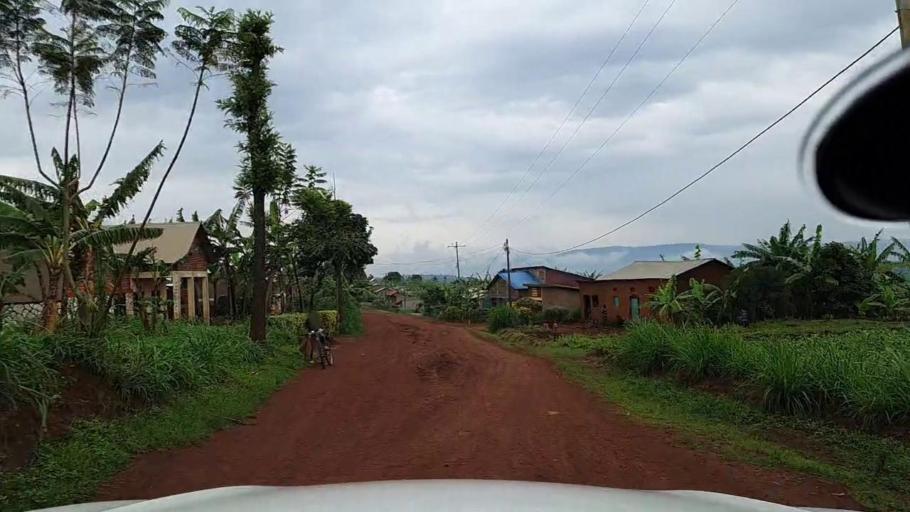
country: RW
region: Kigali
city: Kigali
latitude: -1.9316
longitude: 29.9004
